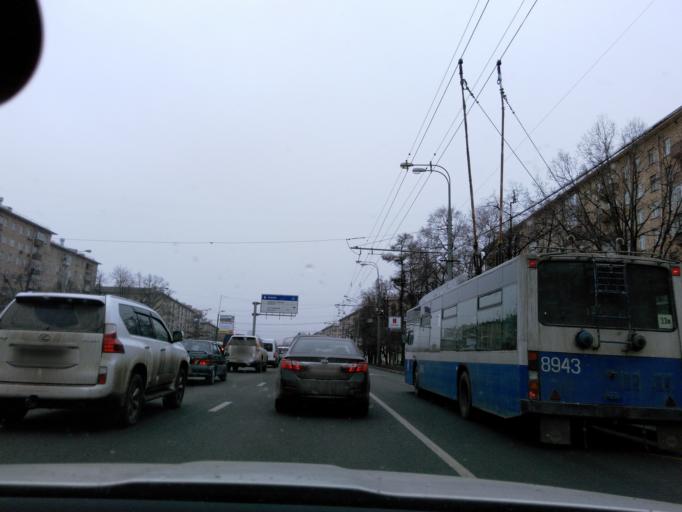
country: RU
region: Moskovskaya
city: Semenovskoye
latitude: 55.6896
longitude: 37.5477
